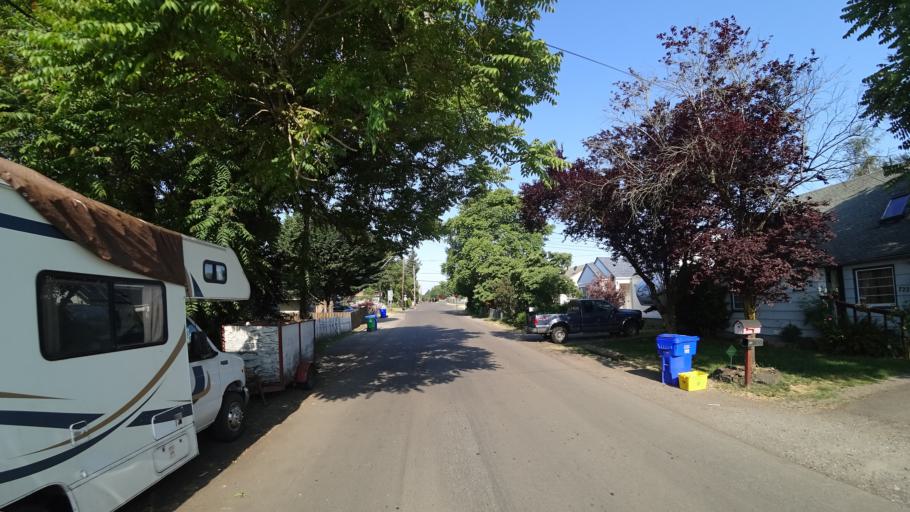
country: US
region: Oregon
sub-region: Multnomah County
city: Lents
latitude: 45.4633
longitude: -122.5885
